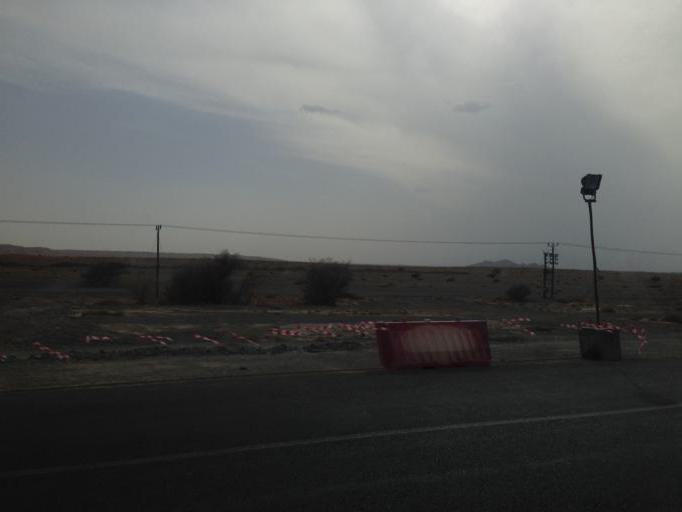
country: OM
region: Ash Sharqiyah
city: Al Qabil
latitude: 22.5399
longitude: 58.7275
